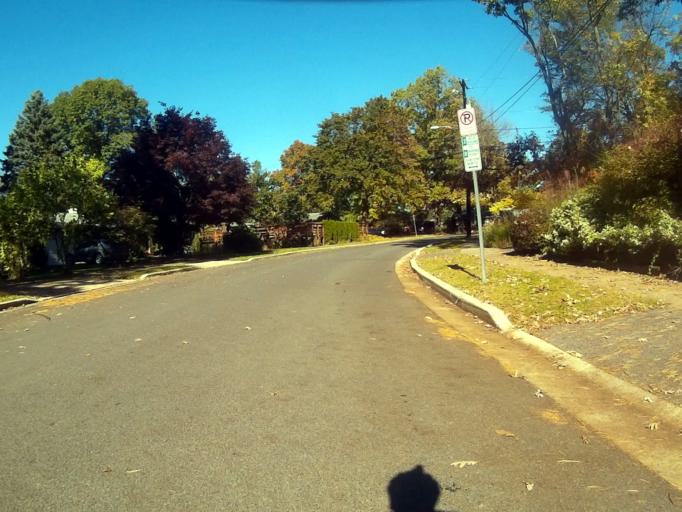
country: US
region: Pennsylvania
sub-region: Centre County
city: State College
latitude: 40.7990
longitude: -77.8789
